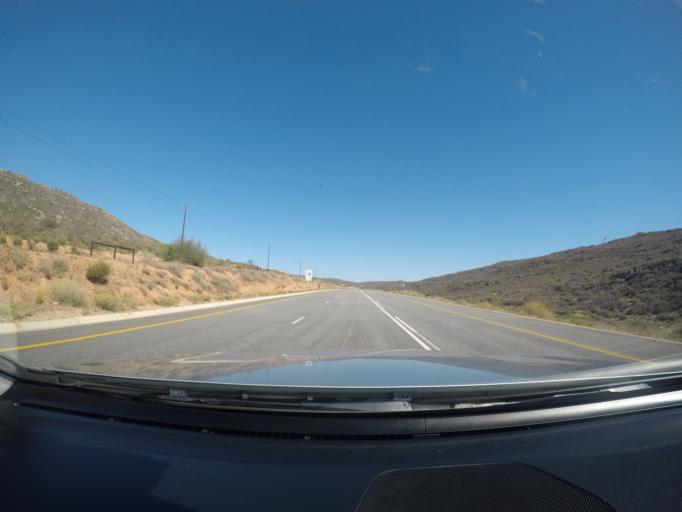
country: ZA
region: Western Cape
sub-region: West Coast District Municipality
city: Clanwilliam
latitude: -32.3461
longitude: 18.9284
